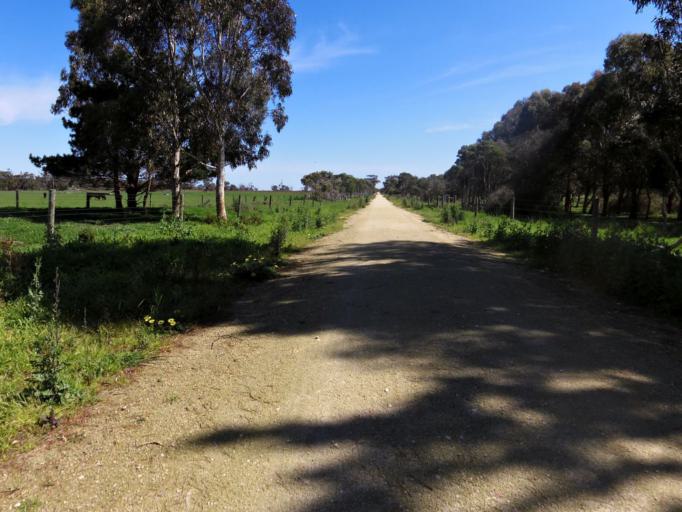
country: AU
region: Victoria
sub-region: Latrobe
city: Morwell
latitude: -38.6676
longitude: 146.4308
